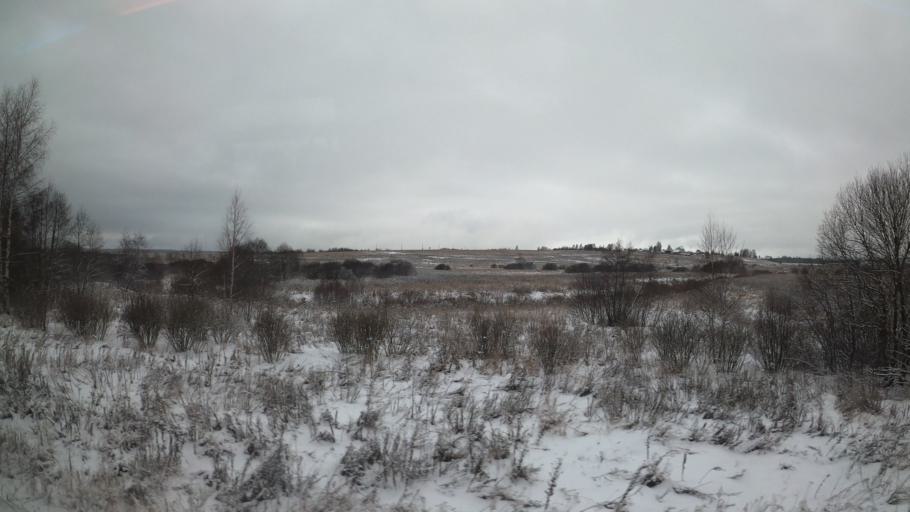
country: RU
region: Jaroslavl
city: Pereslavl'-Zalesskiy
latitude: 56.6940
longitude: 38.9163
